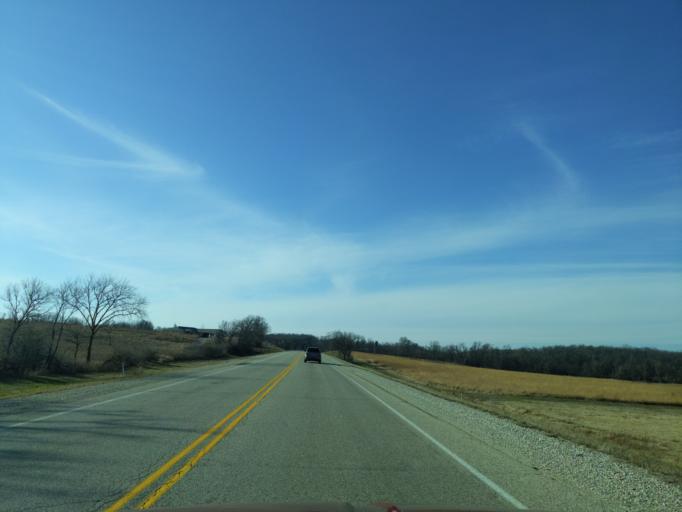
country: US
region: Wisconsin
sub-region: Rock County
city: Milton
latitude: 42.8239
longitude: -88.9356
